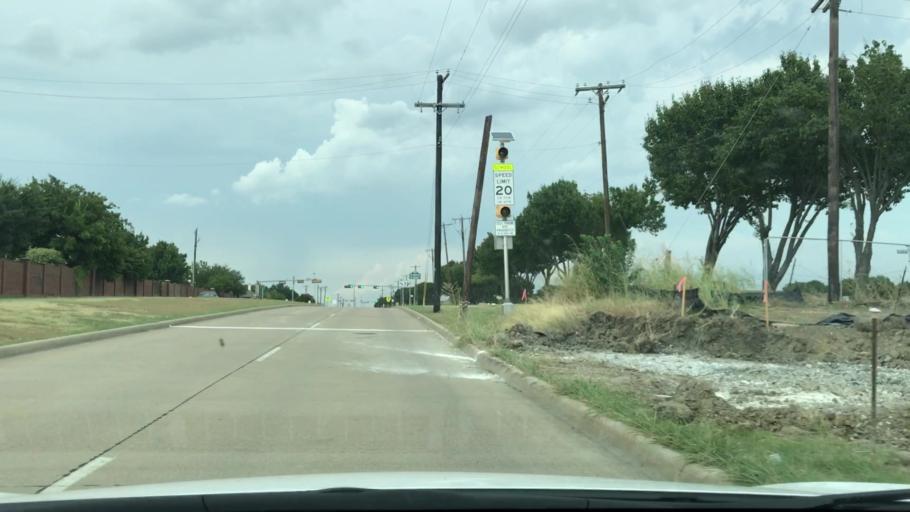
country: US
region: Texas
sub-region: Dallas County
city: Sachse
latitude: 32.9562
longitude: -96.5833
